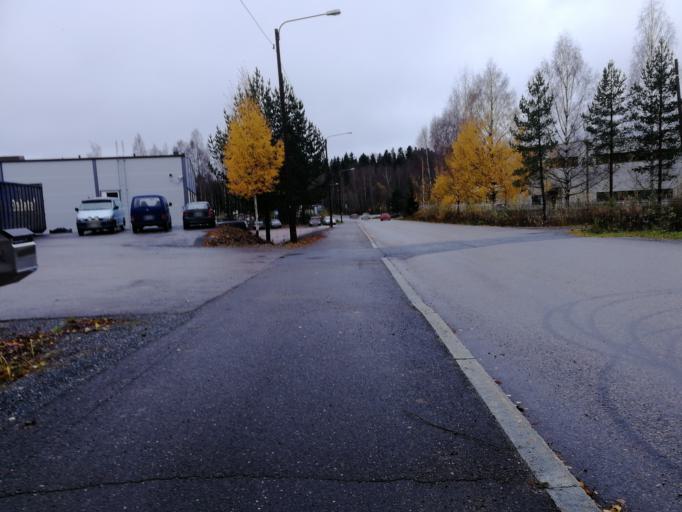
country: FI
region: Pirkanmaa
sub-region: Tampere
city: Tampere
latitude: 61.4547
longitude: 23.8842
